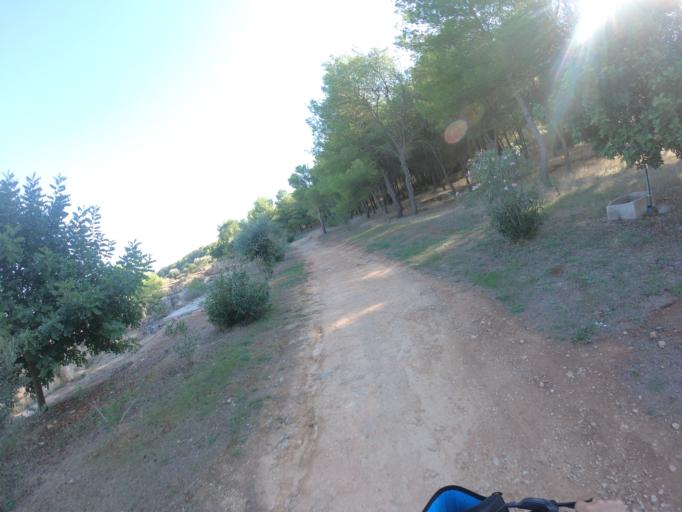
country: IT
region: Apulia
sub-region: Provincia di Lecce
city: Supersano
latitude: 40.0425
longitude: 18.2124
